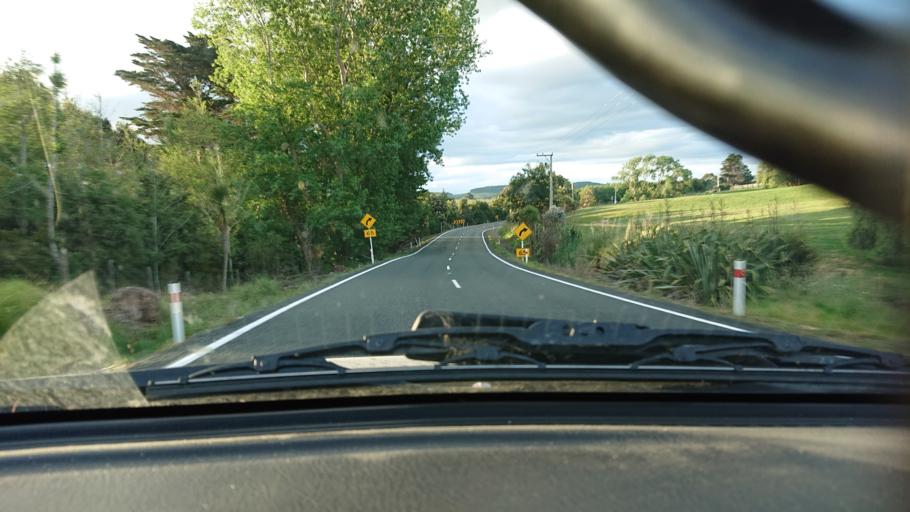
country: NZ
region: Auckland
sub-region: Auckland
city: Parakai
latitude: -36.5228
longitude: 174.4495
